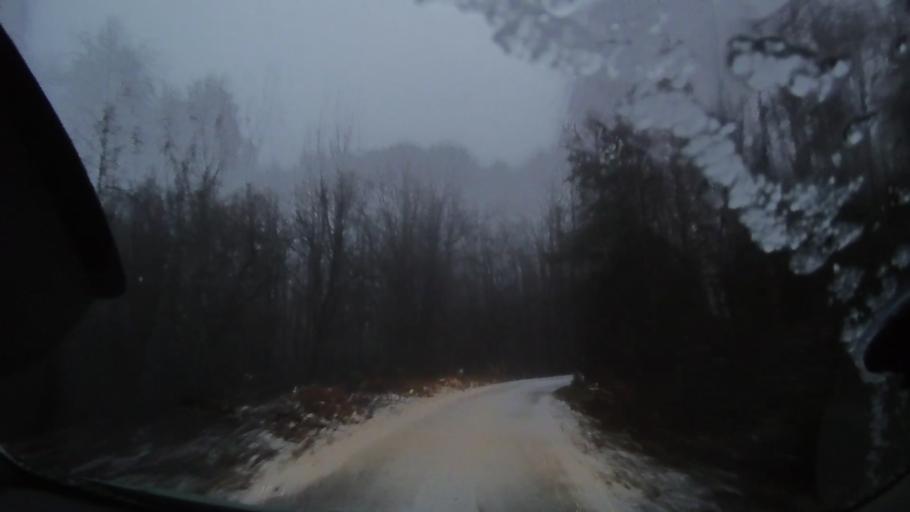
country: RO
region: Alba
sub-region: Comuna Avram Iancu
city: Avram Iancu
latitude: 46.3103
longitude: 22.8004
